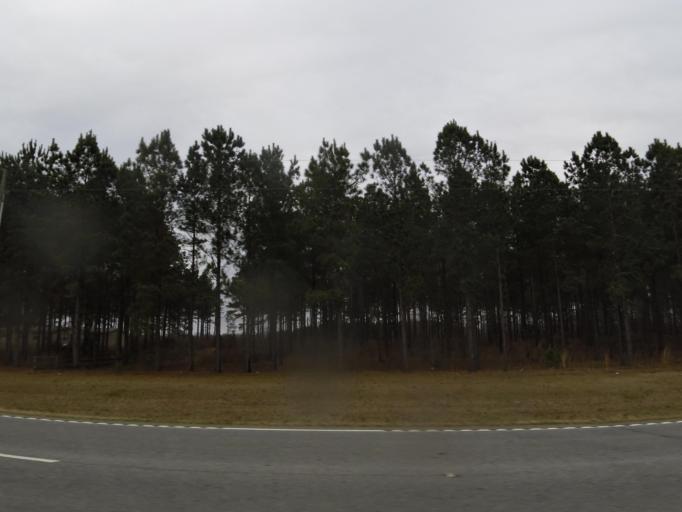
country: US
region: Georgia
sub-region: Randolph County
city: Shellman
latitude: 31.7818
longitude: -84.5908
